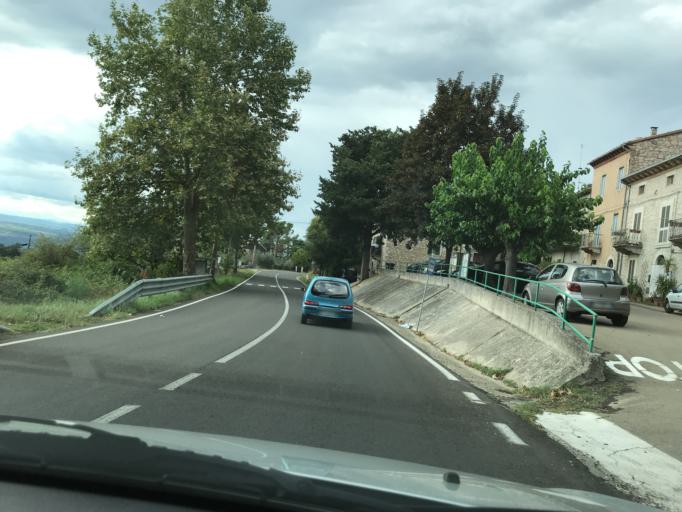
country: IT
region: Umbria
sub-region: Provincia di Terni
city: Guardea
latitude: 42.6326
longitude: 12.2924
